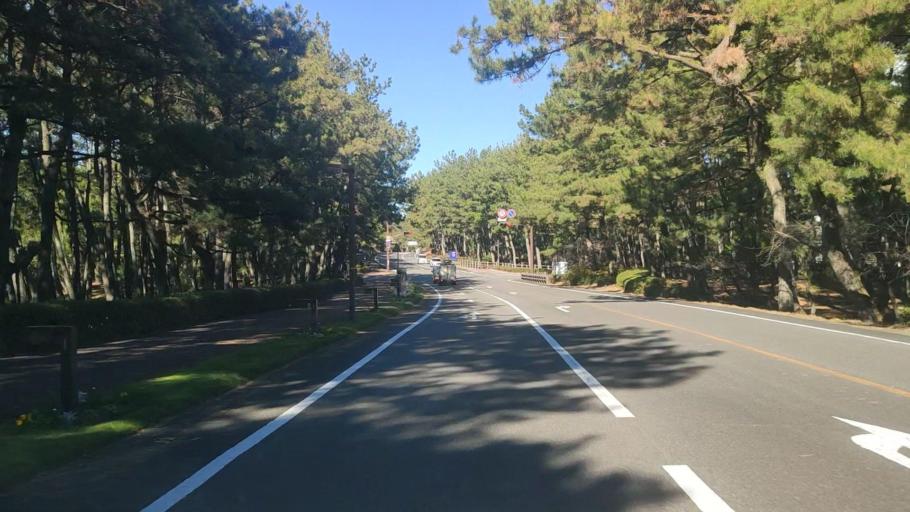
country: JP
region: Miyazaki
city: Miyazaki-shi
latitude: 31.9545
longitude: 131.4672
